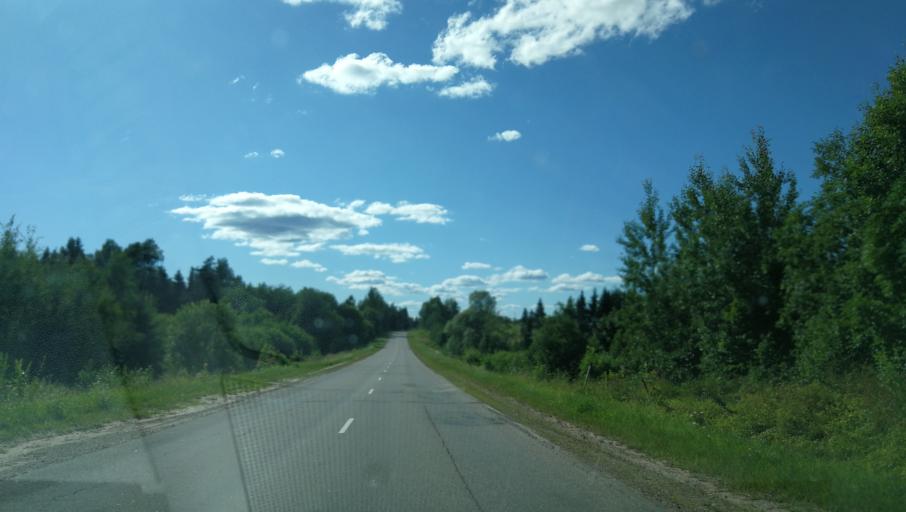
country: LV
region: Madonas Rajons
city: Madona
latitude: 56.8816
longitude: 26.1680
